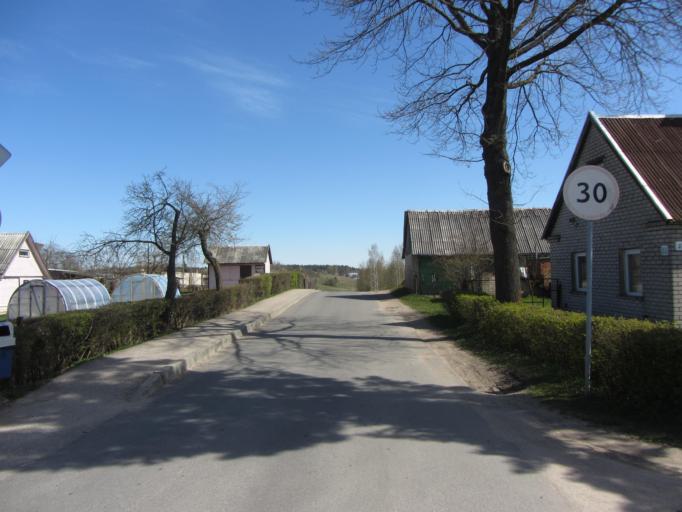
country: LT
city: Zarasai
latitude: 55.7383
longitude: 26.2566
